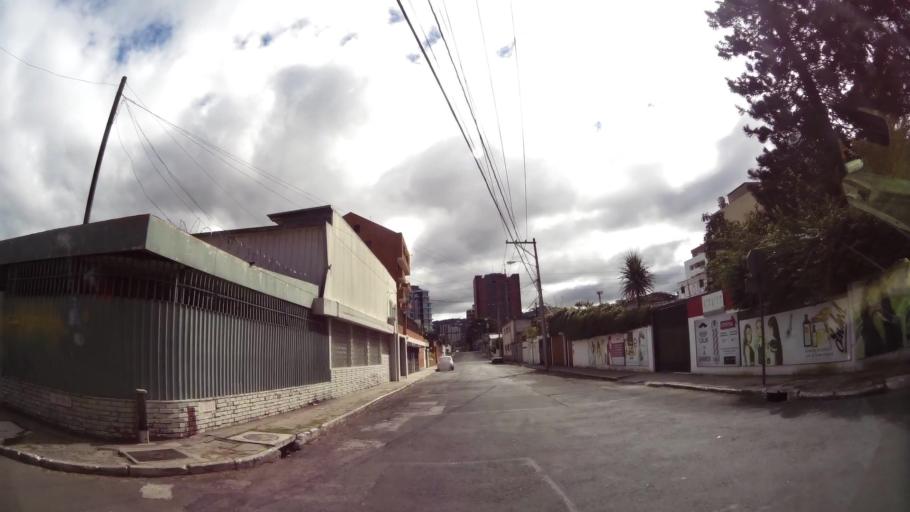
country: GT
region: Guatemala
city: Santa Catarina Pinula
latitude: 14.5928
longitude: -90.5077
